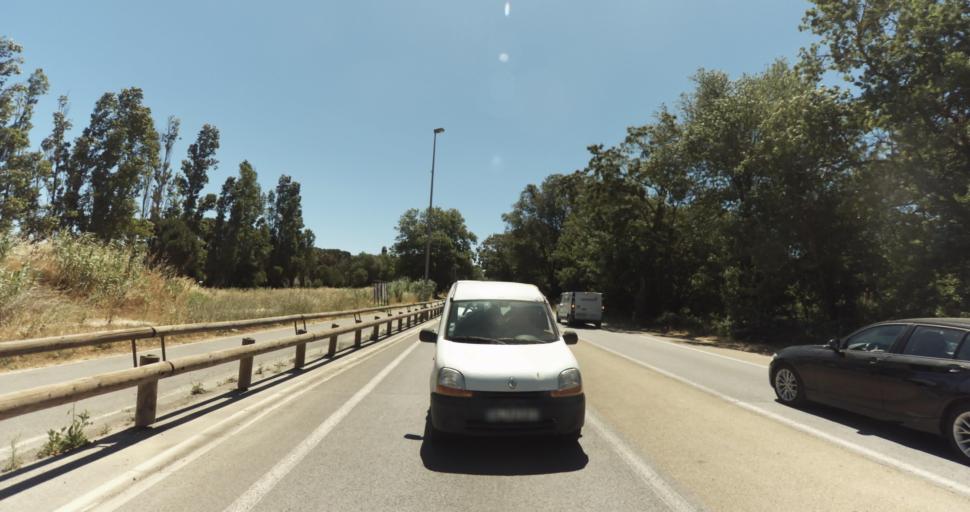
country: FR
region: Provence-Alpes-Cote d'Azur
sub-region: Departement du Var
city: Gassin
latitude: 43.2612
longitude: 6.5877
